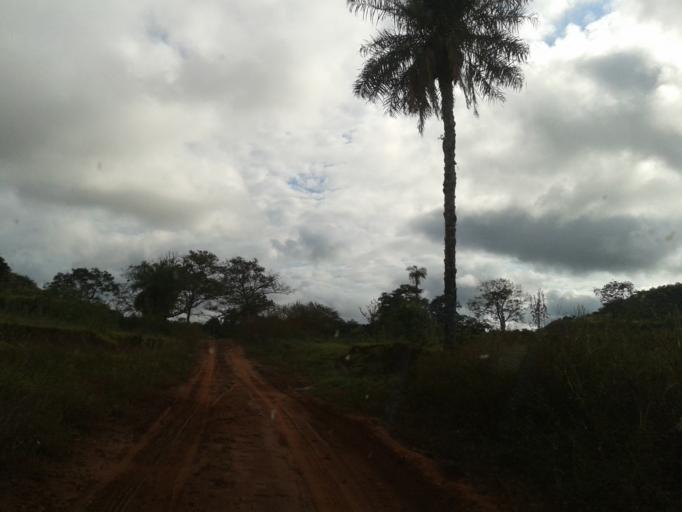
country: BR
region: Minas Gerais
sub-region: Campina Verde
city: Campina Verde
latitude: -19.5000
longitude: -49.6052
